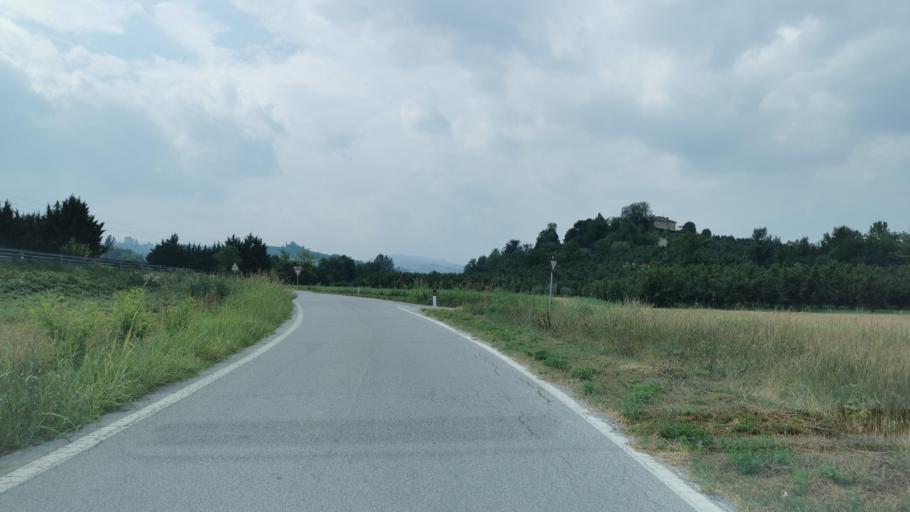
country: IT
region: Piedmont
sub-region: Provincia di Cuneo
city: Roddi
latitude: 44.6785
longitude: 7.9842
